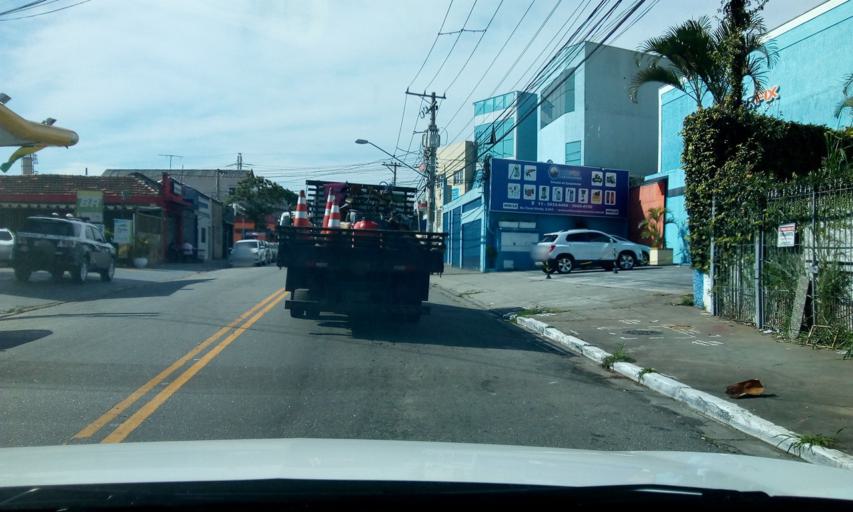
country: BR
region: Sao Paulo
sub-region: Sao Paulo
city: Sao Paulo
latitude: -23.5064
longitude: -46.6640
